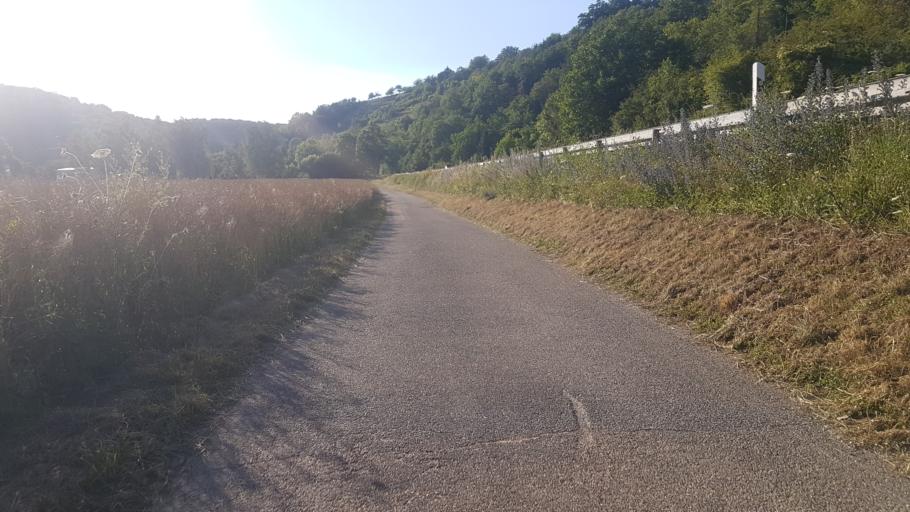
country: DE
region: Baden-Wuerttemberg
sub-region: Regierungsbezirk Stuttgart
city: Neudenau
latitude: 49.3016
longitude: 9.3155
